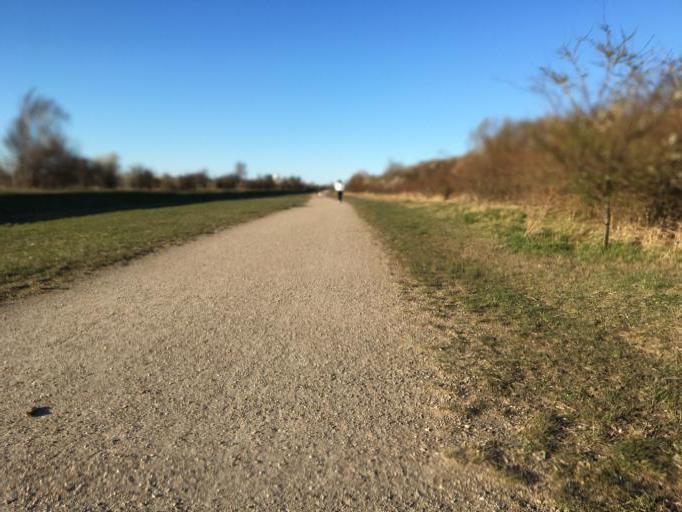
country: DK
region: Capital Region
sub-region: Tarnby Kommune
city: Tarnby
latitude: 55.5965
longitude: 12.5733
